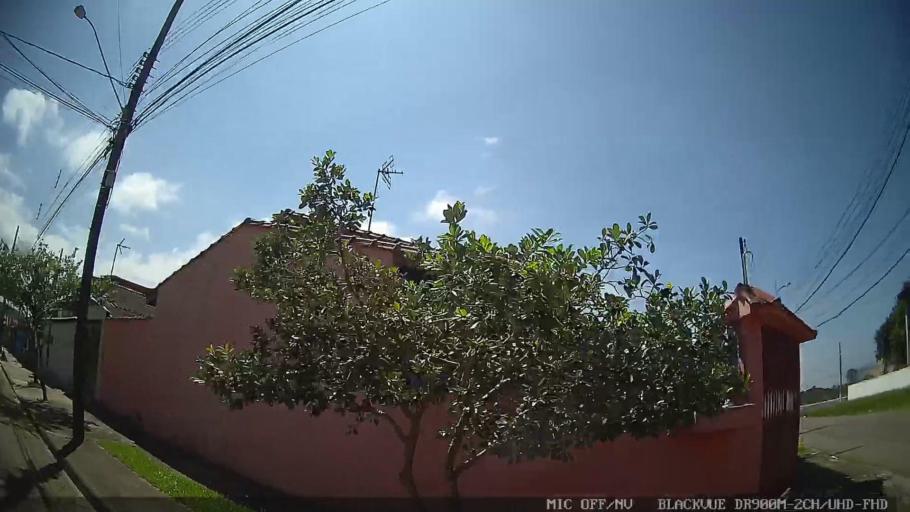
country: BR
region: Sao Paulo
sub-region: Peruibe
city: Peruibe
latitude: -24.3038
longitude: -47.0035
